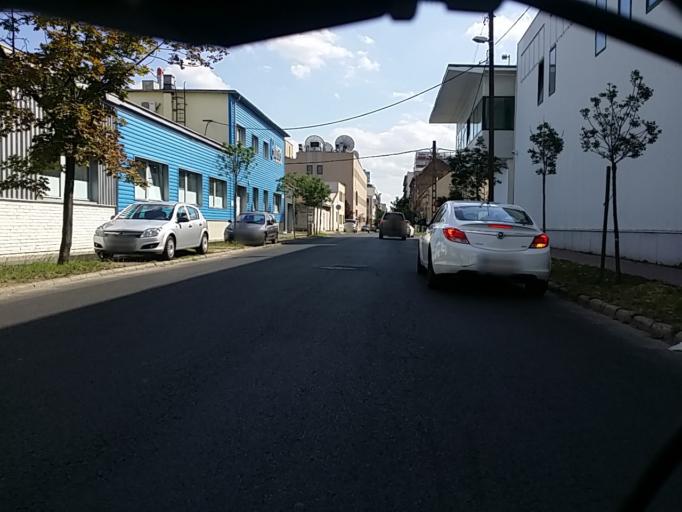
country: HU
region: Budapest
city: Budapest XIII. keruelet
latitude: 47.5384
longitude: 19.0712
